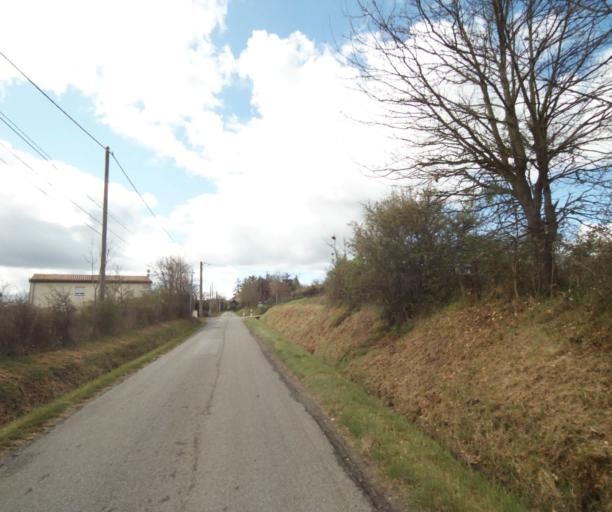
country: FR
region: Midi-Pyrenees
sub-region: Departement de l'Ariege
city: Saverdun
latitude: 43.2113
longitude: 1.5758
